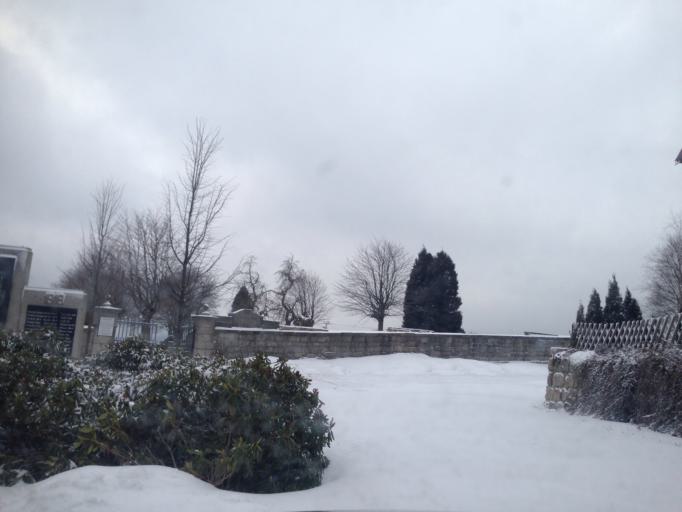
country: CZ
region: Liberecky
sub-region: Okres Jablonec nad Nisou
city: Korenov
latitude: 50.7418
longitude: 15.3493
